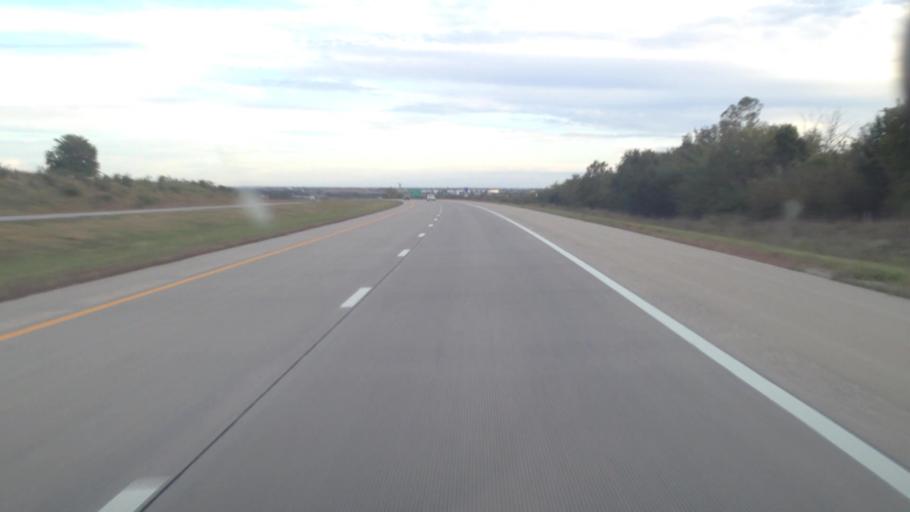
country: US
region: Kansas
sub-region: Franklin County
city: Ottawa
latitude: 38.6793
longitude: -95.2634
